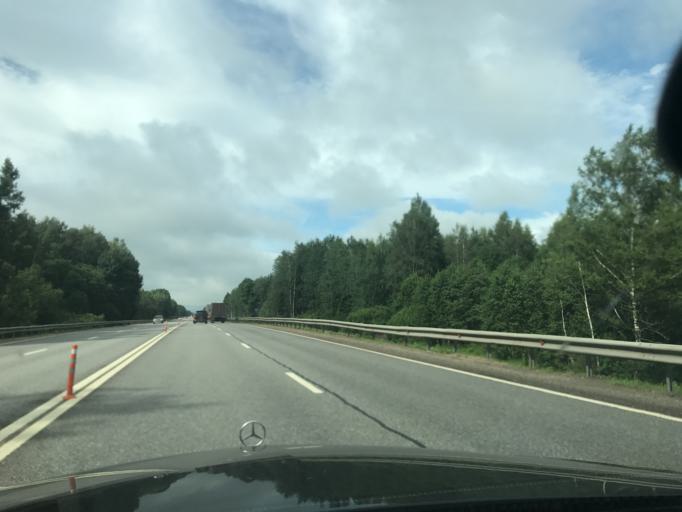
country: RU
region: Smolensk
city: Kardymovo
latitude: 55.0077
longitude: 32.2854
